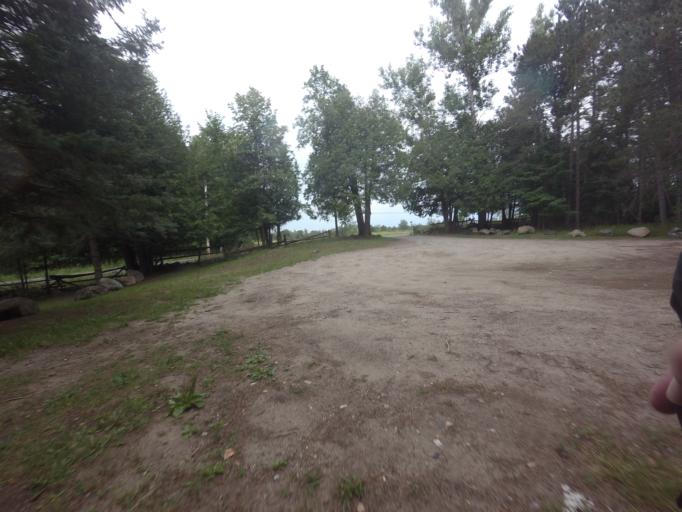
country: CA
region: Ontario
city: Perth
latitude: 45.0627
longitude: -76.3931
